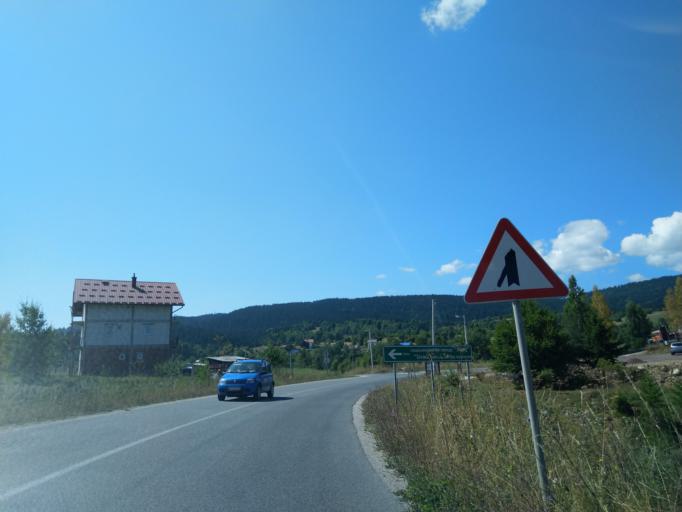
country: RS
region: Central Serbia
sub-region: Zlatiborski Okrug
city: Nova Varos
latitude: 43.4273
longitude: 19.8305
